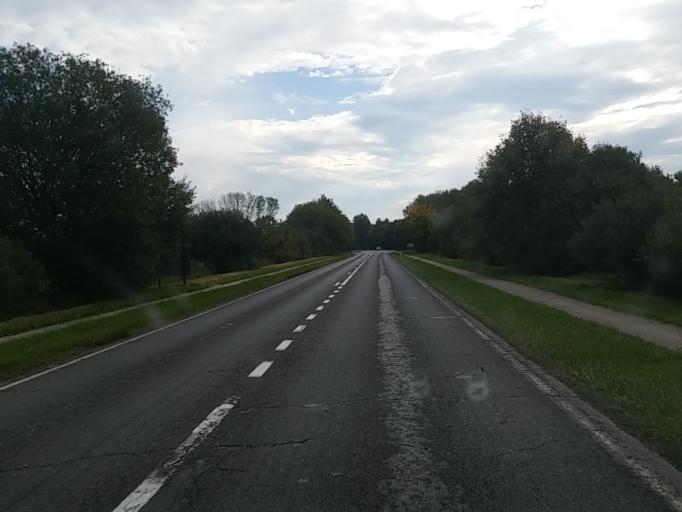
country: BE
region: Wallonia
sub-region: Province du Luxembourg
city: Etalle
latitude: 49.6729
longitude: 5.5781
